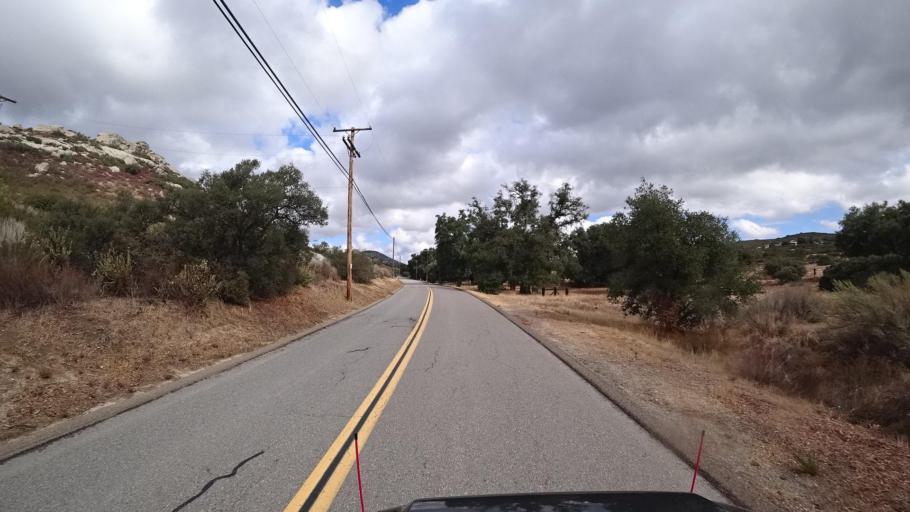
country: US
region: California
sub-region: San Diego County
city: Campo
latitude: 32.6490
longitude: -116.4234
